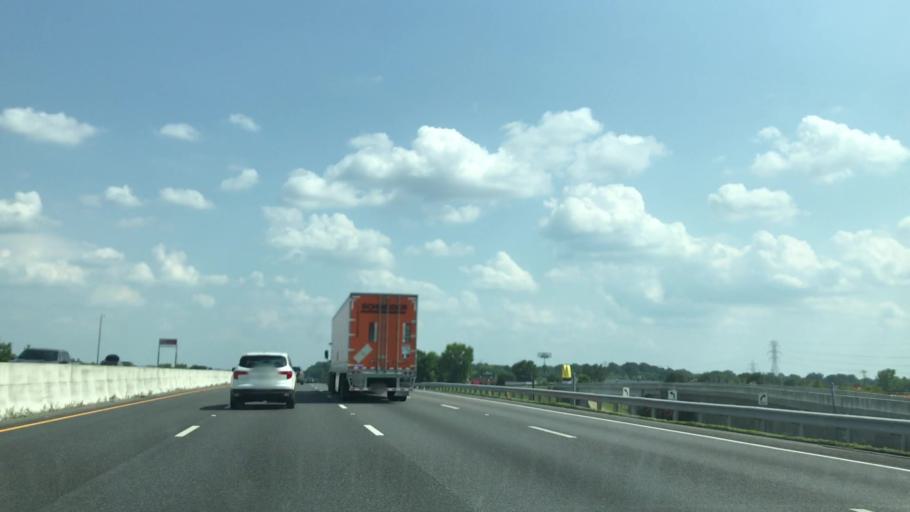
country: US
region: South Carolina
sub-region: York County
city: India Hook
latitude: 34.9748
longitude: -80.9874
